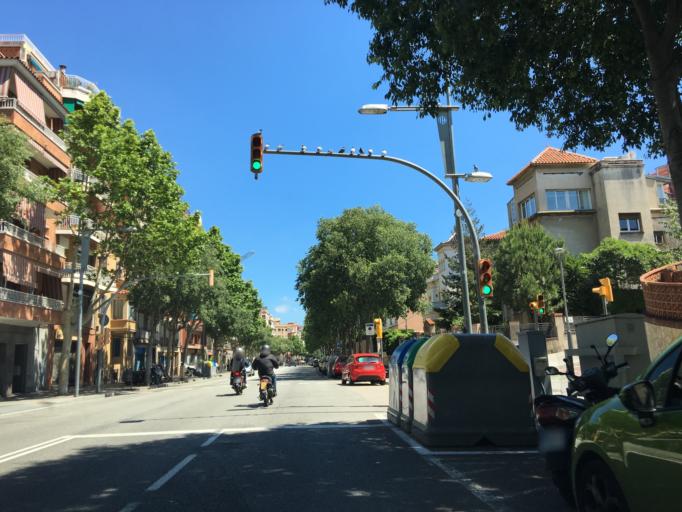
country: ES
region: Catalonia
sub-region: Provincia de Barcelona
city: Horta-Guinardo
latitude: 41.4276
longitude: 2.1670
